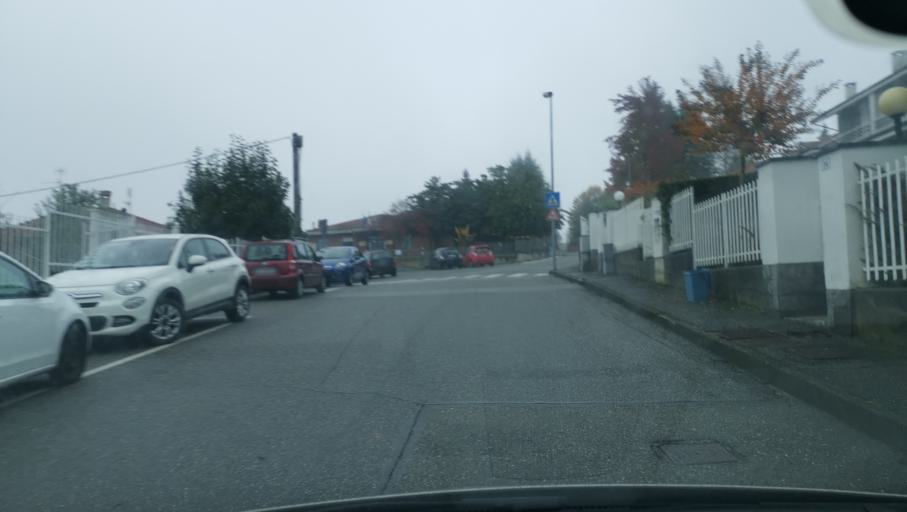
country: IT
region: Piedmont
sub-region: Provincia di Torino
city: Gassino Torinese
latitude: 45.1224
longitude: 7.8193
